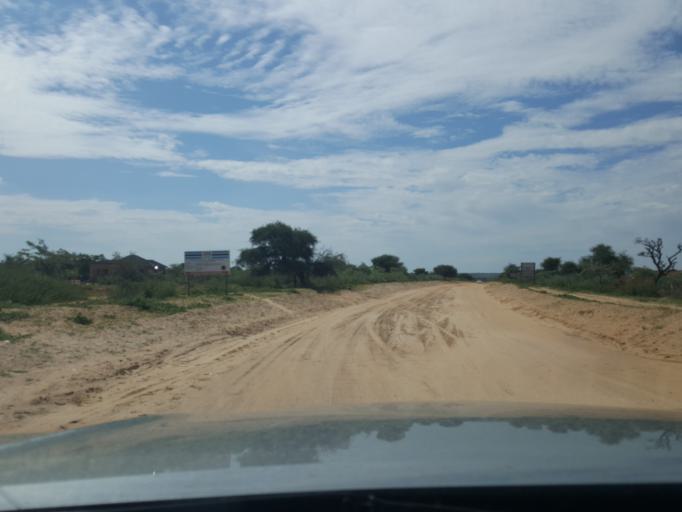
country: BW
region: Kweneng
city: Letlhakeng
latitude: -24.0780
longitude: 25.0299
